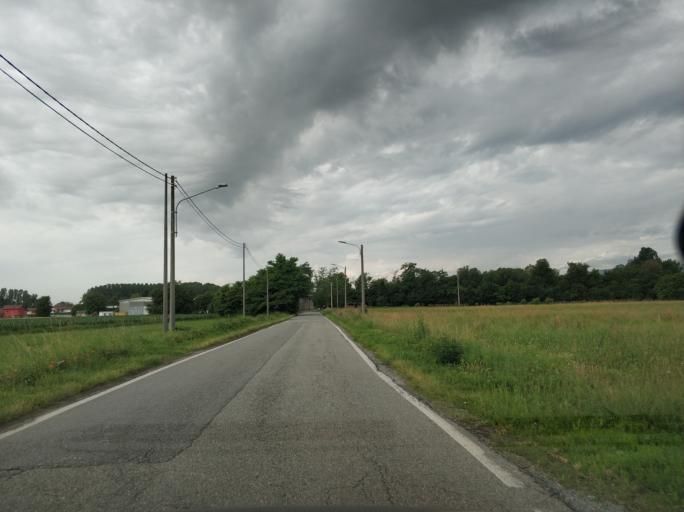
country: IT
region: Piedmont
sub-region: Provincia di Torino
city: San Maurizio
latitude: 45.1943
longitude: 7.6155
